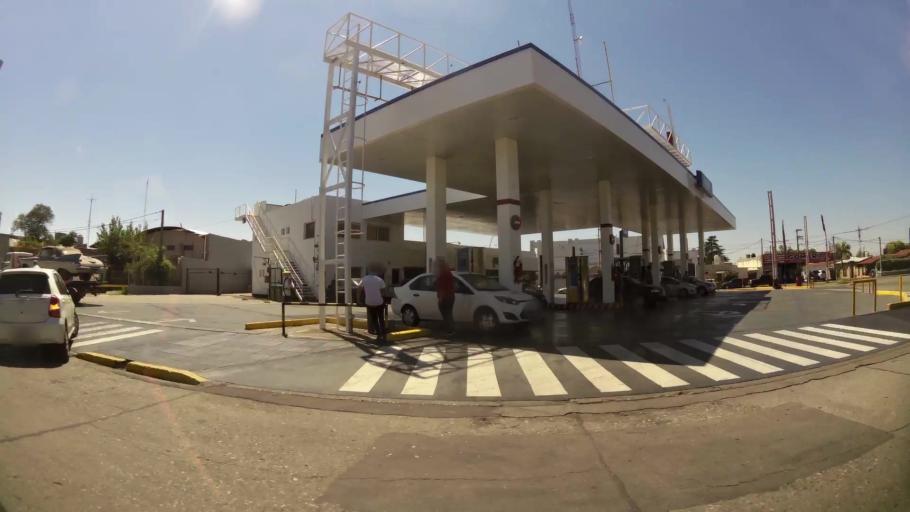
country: AR
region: Cordoba
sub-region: Departamento de Capital
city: Cordoba
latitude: -31.4287
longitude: -64.2107
